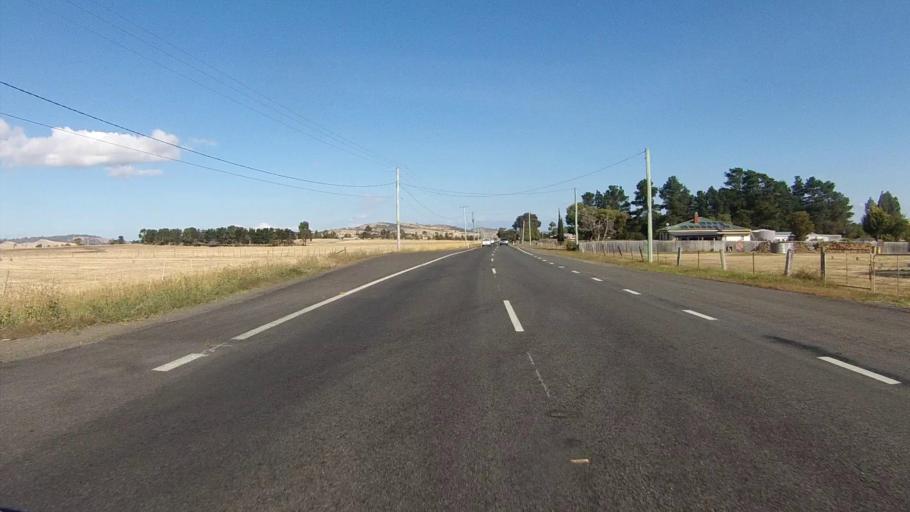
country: AU
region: Tasmania
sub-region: Sorell
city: Sorell
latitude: -42.7307
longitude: 147.5270
